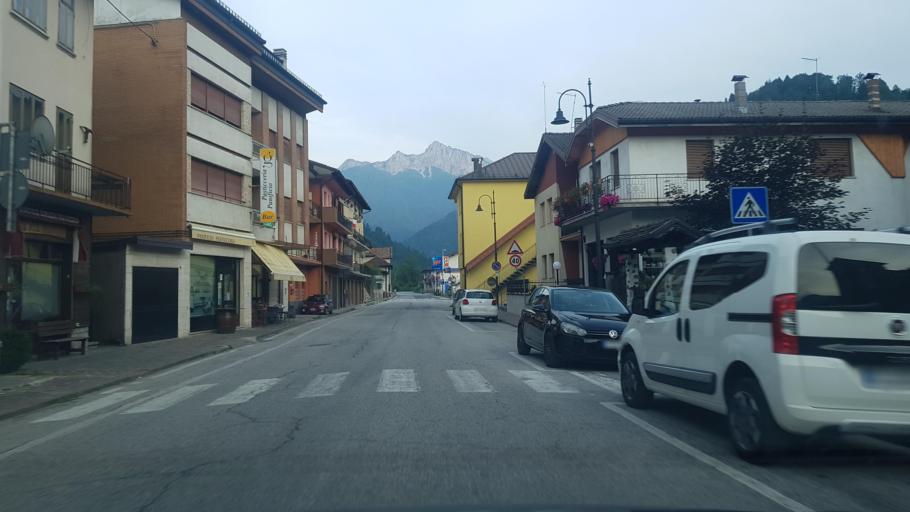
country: IT
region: Friuli Venezia Giulia
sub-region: Provincia di Udine
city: Paularo
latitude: 46.5285
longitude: 13.1184
